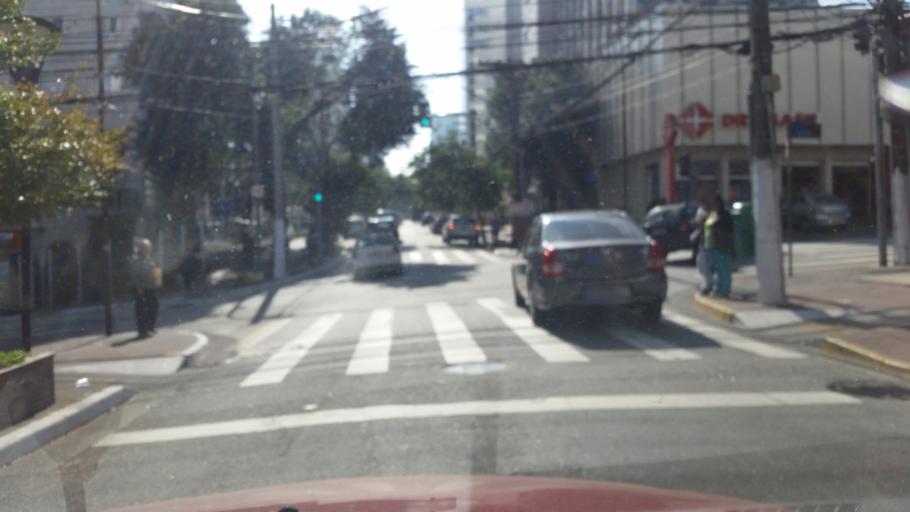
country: BR
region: Sao Paulo
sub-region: Diadema
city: Diadema
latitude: -23.6245
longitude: -46.6835
